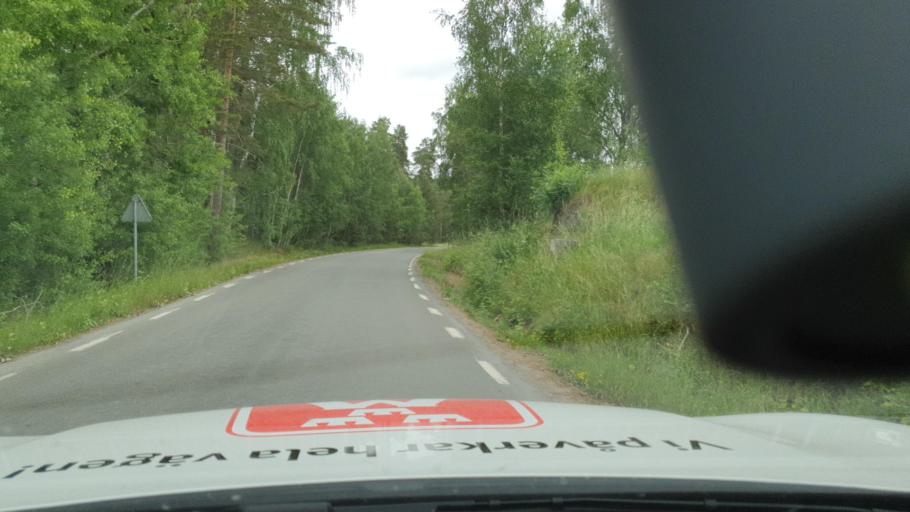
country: SE
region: Vaestra Goetaland
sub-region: Tidaholms Kommun
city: Olofstorp
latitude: 58.2348
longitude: 14.0982
